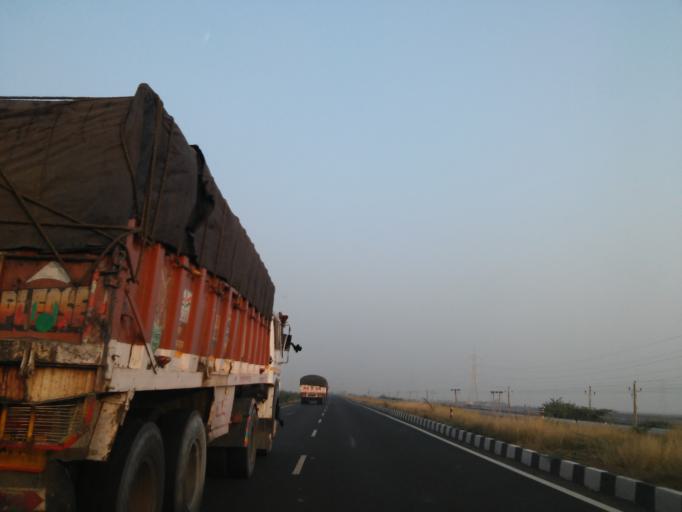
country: IN
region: Gujarat
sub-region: Rajkot
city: Morbi
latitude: 23.1556
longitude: 70.7383
